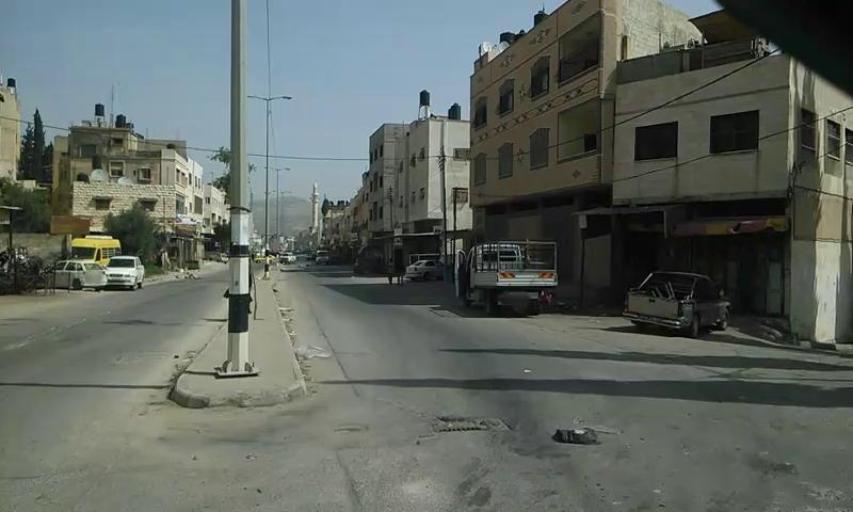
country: PS
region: West Bank
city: Balatah
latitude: 32.2187
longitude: 35.2942
